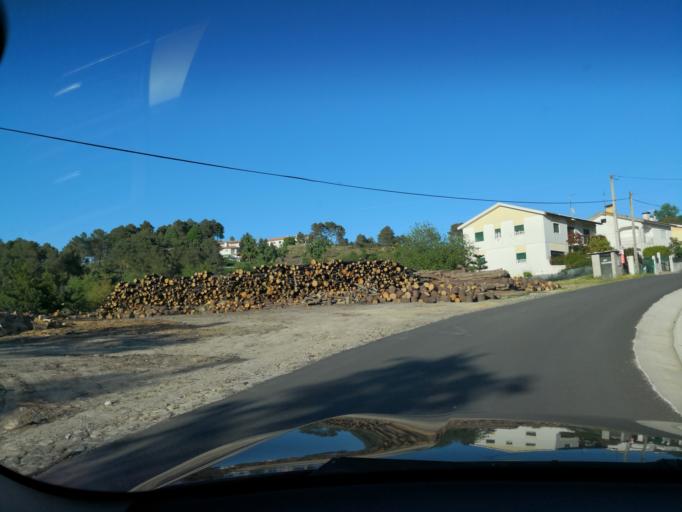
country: PT
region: Vila Real
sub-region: Vila Real
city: Vila Real
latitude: 41.3369
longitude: -7.7298
